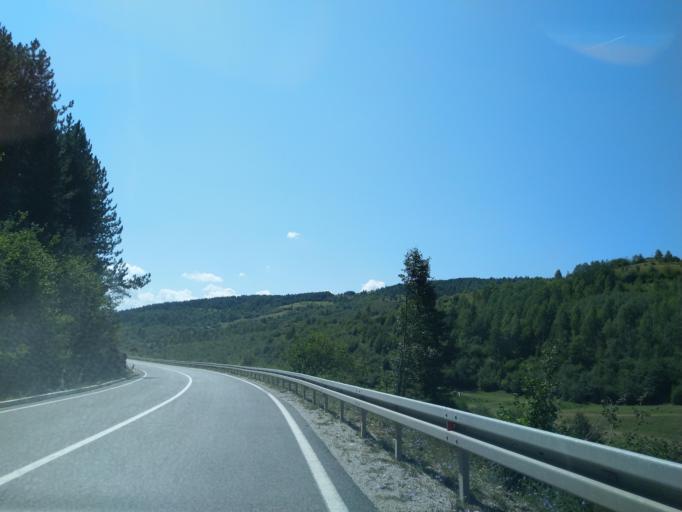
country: RS
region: Central Serbia
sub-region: Zlatiborski Okrug
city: Sjenica
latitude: 43.2891
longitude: 19.9423
